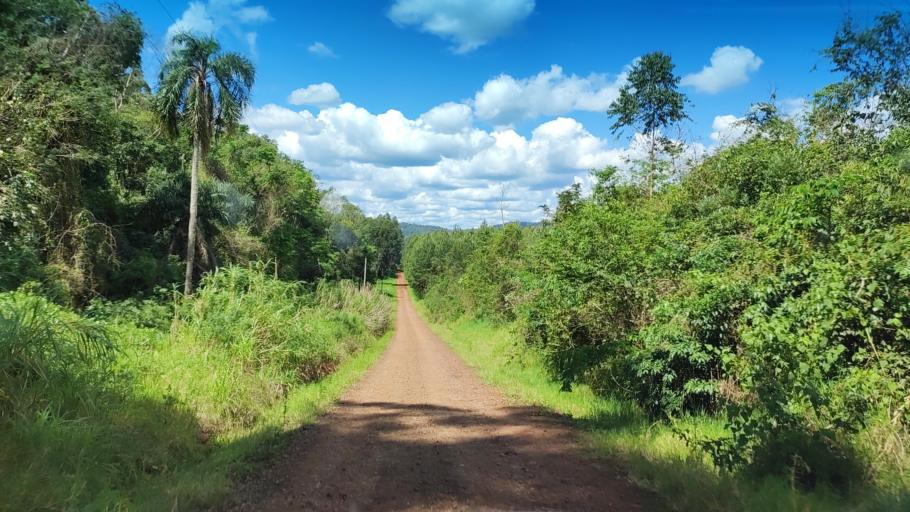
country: AR
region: Misiones
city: Ruiz de Montoya
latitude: -26.9528
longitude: -55.0185
